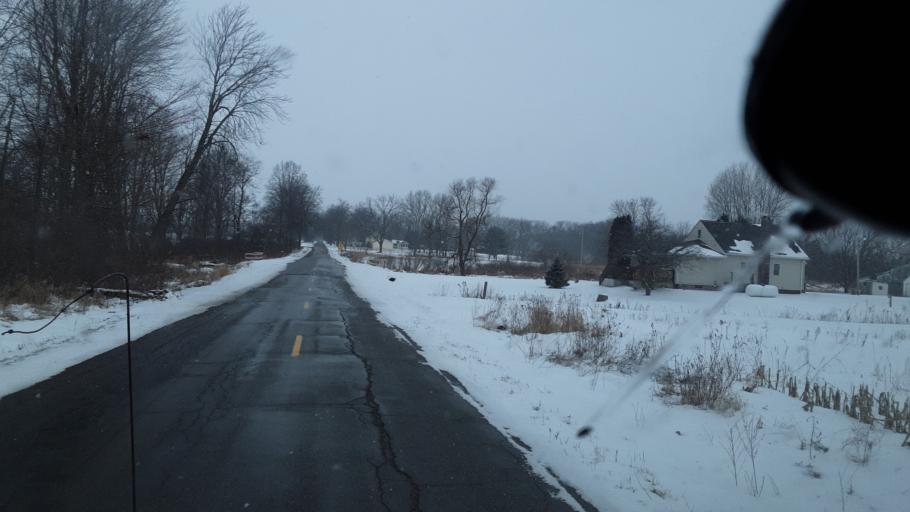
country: US
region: Michigan
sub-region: Ingham County
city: Leslie
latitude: 42.4366
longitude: -84.4736
